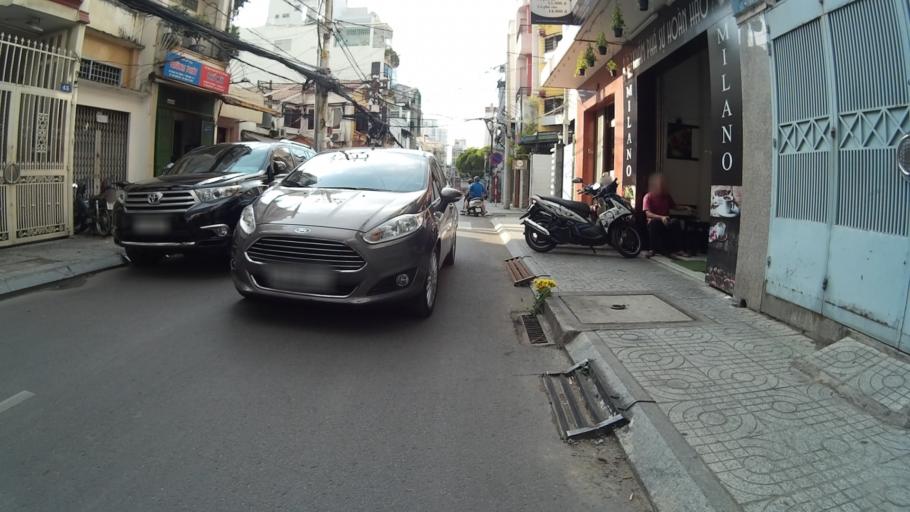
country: VN
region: Ho Chi Minh City
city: Quan Mot
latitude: 10.7904
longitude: 106.6925
